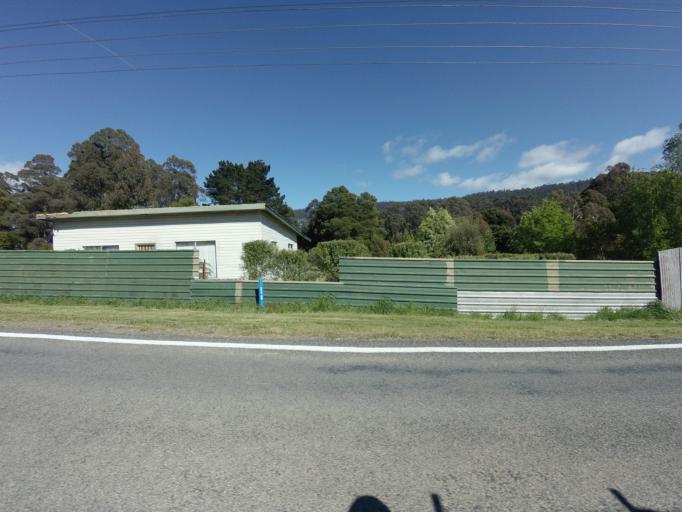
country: AU
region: Tasmania
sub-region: Derwent Valley
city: New Norfolk
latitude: -42.6876
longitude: 146.7180
